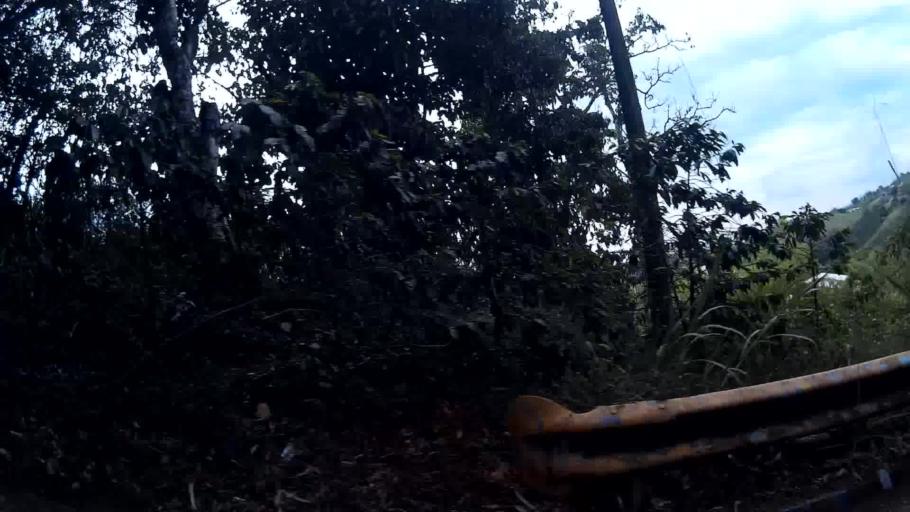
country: CO
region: Valle del Cauca
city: Ulloa
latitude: 4.7232
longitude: -75.7156
